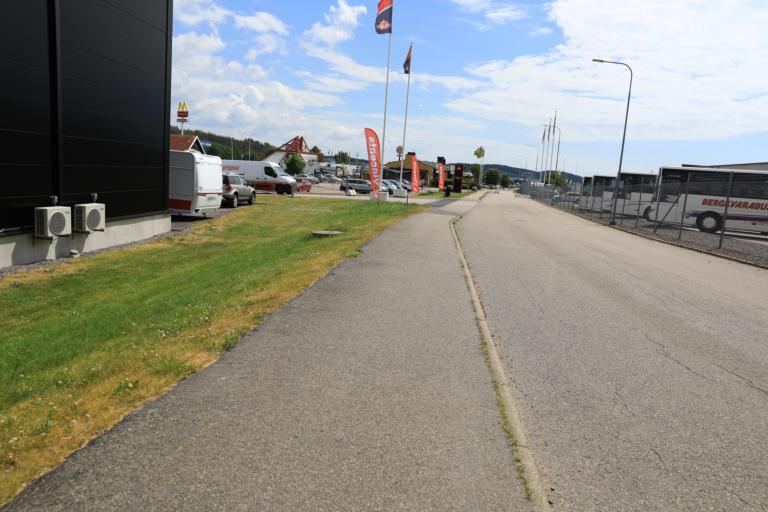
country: SE
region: Halland
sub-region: Varbergs Kommun
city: Varberg
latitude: 57.1701
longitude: 12.2758
